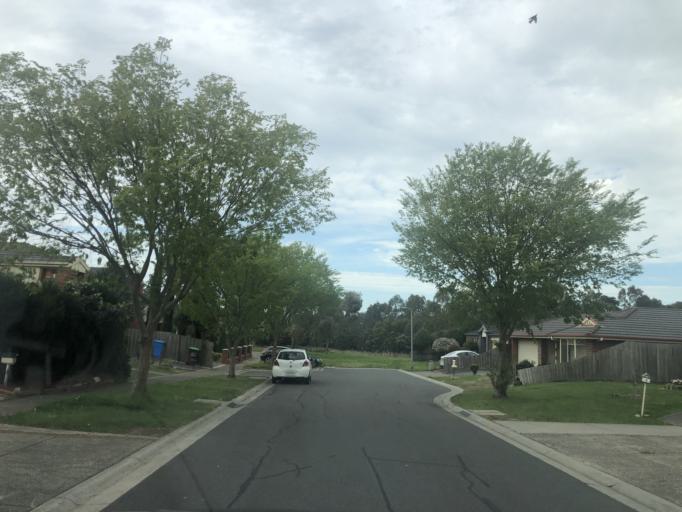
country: AU
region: Victoria
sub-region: Casey
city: Hallam
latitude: -38.0035
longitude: 145.2873
